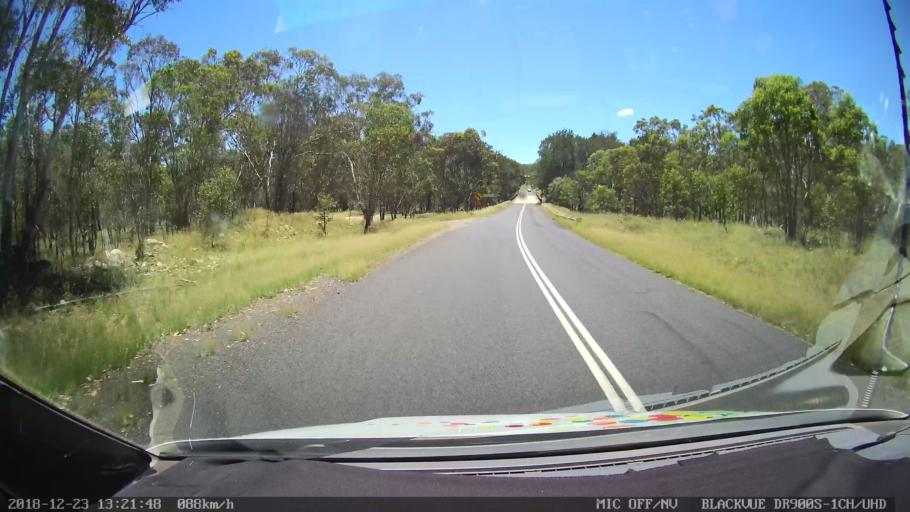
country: AU
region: New South Wales
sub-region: Armidale Dumaresq
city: Armidale
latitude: -30.4801
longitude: 151.4288
